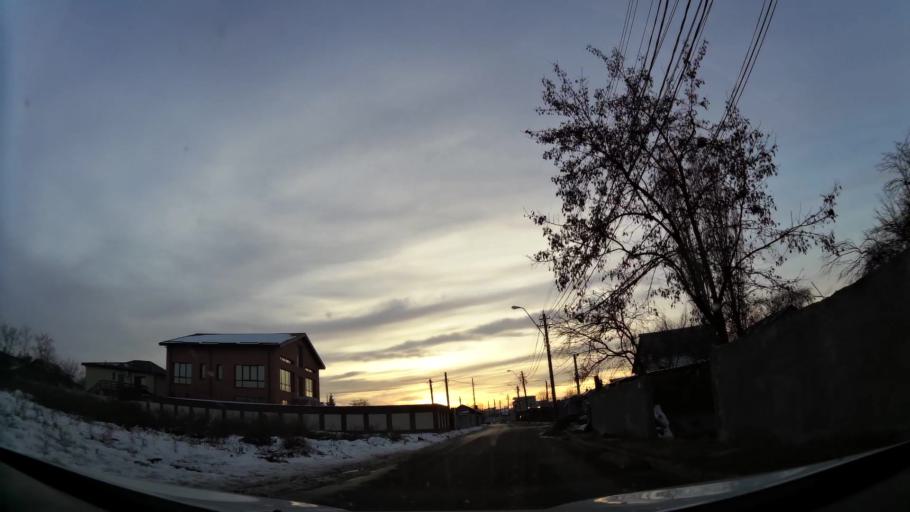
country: RO
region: Ilfov
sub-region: Comuna Magurele
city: Magurele
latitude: 44.3917
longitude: 26.0320
